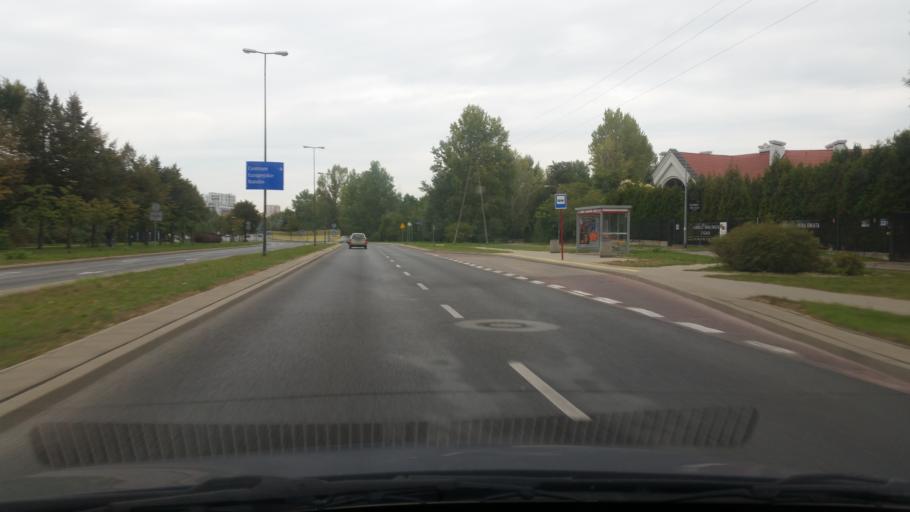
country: PL
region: Masovian Voivodeship
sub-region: Warszawa
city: Kabaty
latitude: 52.1366
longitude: 21.0725
